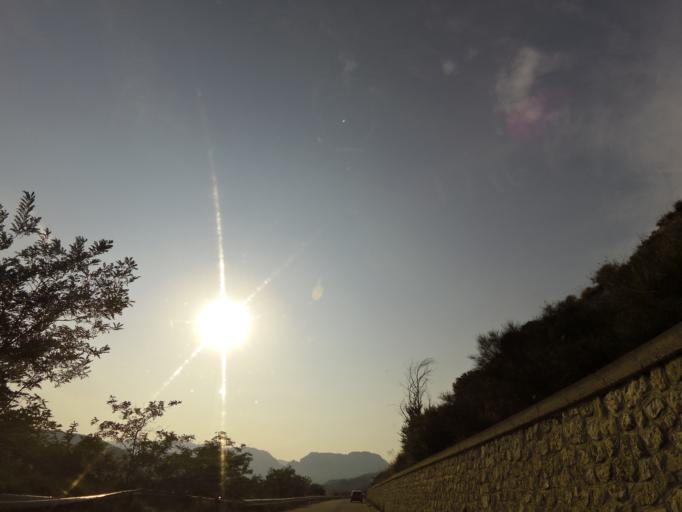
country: IT
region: Calabria
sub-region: Provincia di Reggio Calabria
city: Monasterace
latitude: 38.4624
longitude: 16.5178
